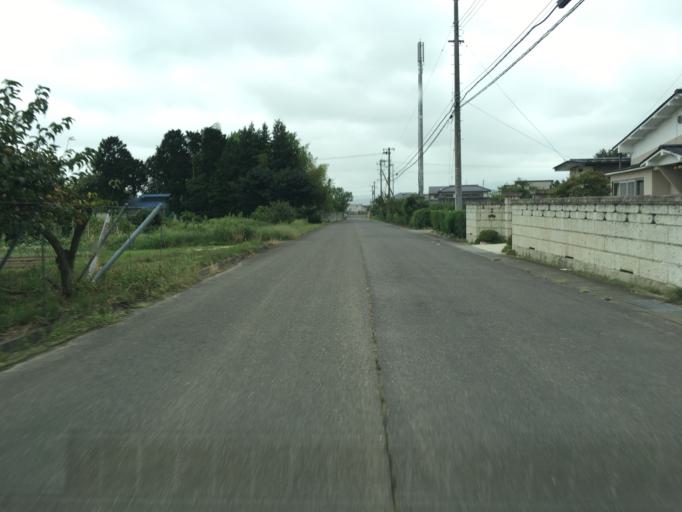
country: JP
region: Fukushima
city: Fukushima-shi
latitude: 37.7747
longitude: 140.3836
